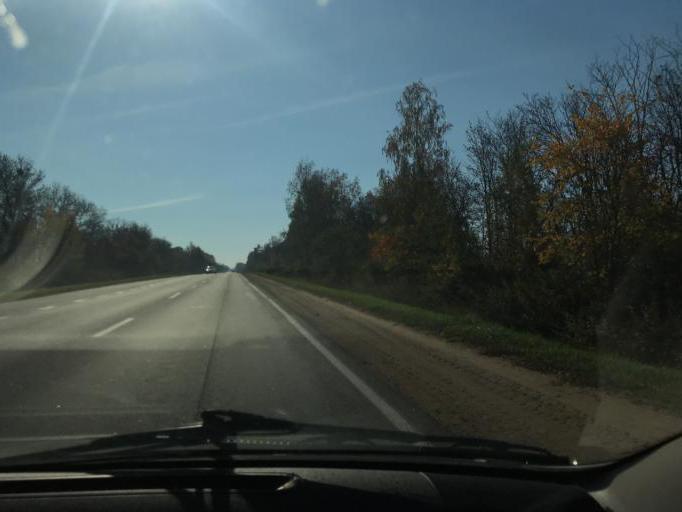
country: BY
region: Minsk
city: Starobin
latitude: 52.7958
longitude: 27.4646
